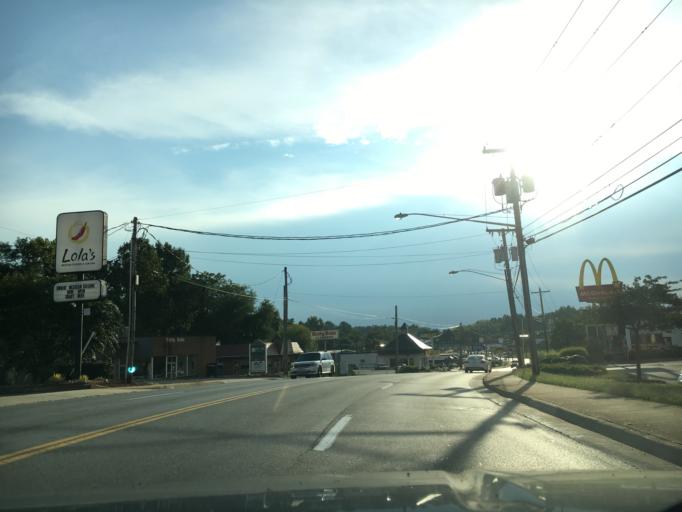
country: US
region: Virginia
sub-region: City of Lynchburg
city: West Lynchburg
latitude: 37.4148
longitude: -79.2074
